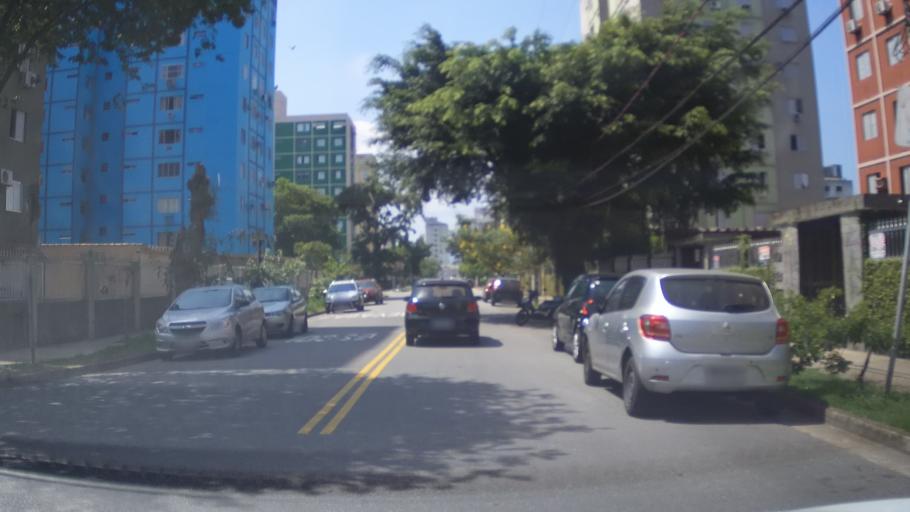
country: BR
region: Sao Paulo
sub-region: Santos
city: Santos
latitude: -23.9743
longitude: -46.3100
